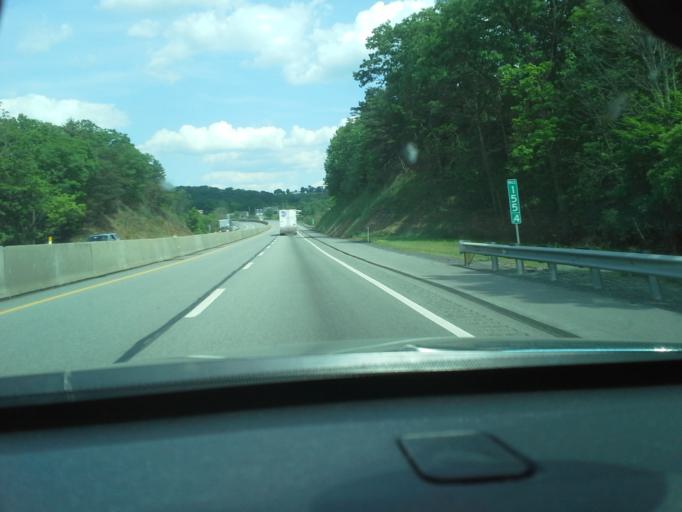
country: US
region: Pennsylvania
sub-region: Bedford County
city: Earlston
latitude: 40.0014
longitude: -78.3639
